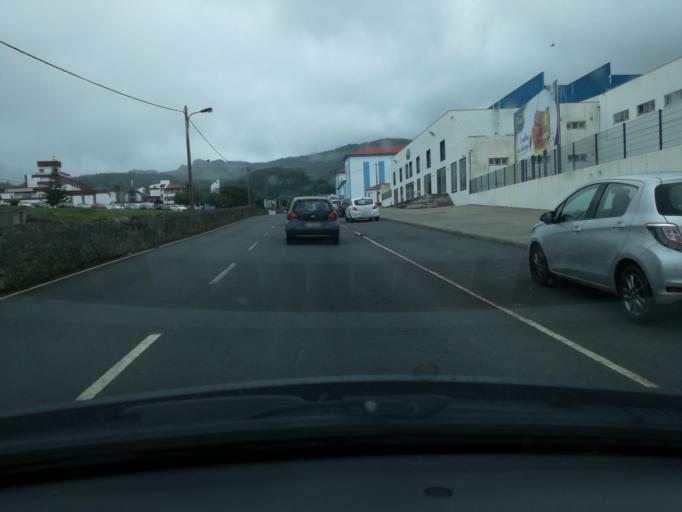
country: PT
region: Azores
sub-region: Angra do Heroismo
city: Angra do Heroismo
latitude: 38.6686
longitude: -27.2153
